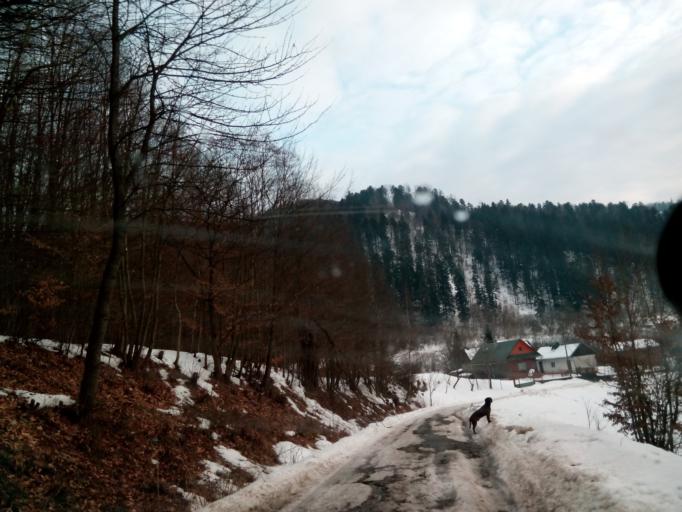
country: SK
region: Presovsky
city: Sabinov
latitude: 49.1956
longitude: 21.0895
